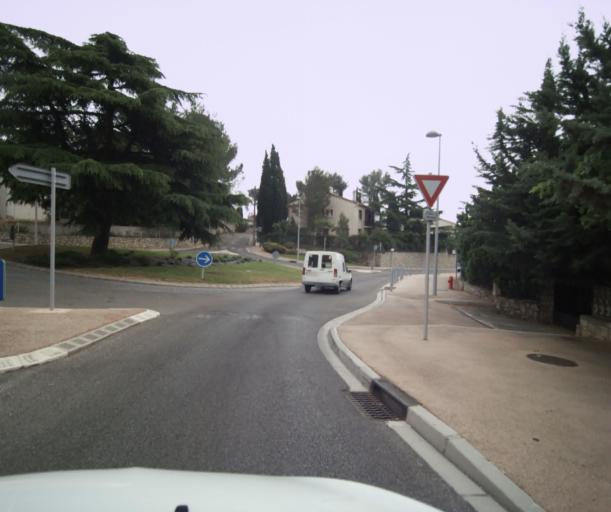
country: FR
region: Provence-Alpes-Cote d'Azur
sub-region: Departement du Var
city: La Garde
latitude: 43.1272
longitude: 5.9991
